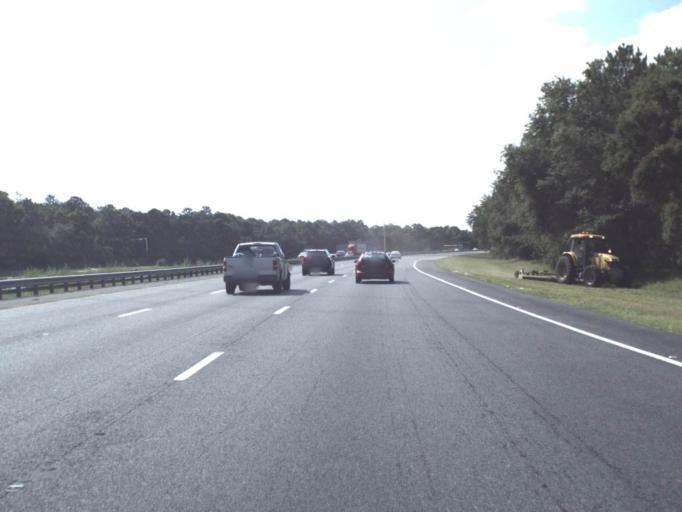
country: US
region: Florida
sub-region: Flagler County
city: Palm Coast
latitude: 29.6595
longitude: -81.2827
